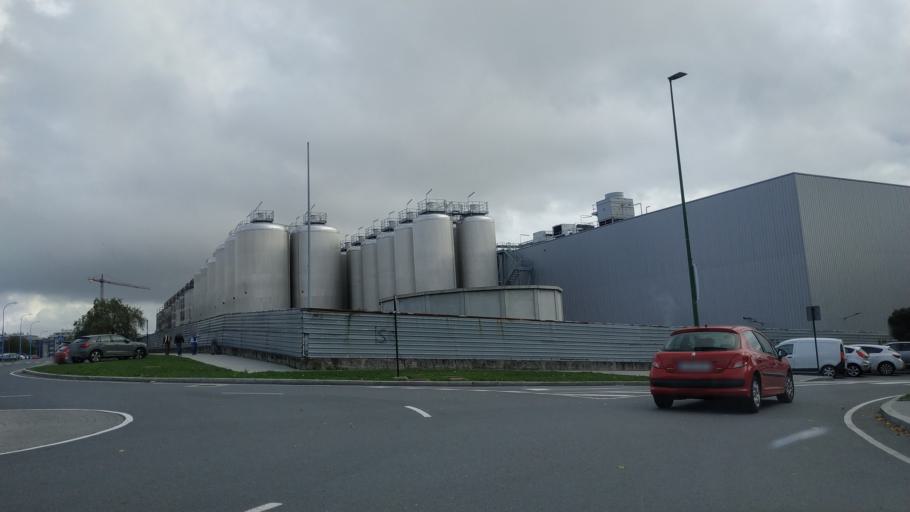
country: ES
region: Galicia
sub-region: Provincia da Coruna
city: A Coruna
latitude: 43.3544
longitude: -8.4219
